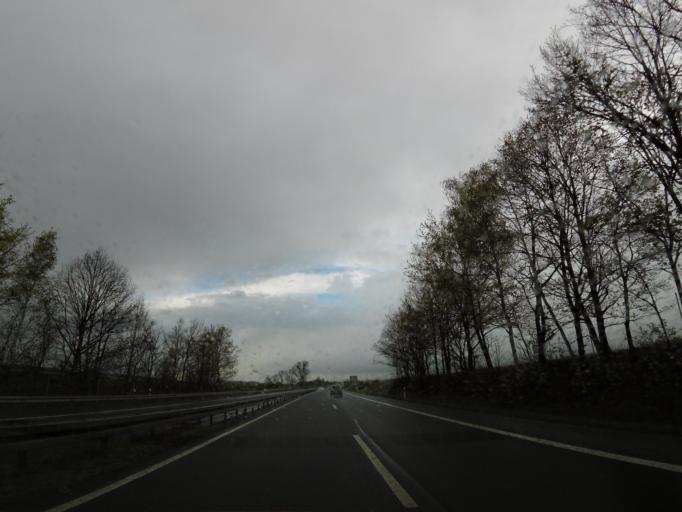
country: DE
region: Lower Saxony
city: Vienenburg
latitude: 51.9244
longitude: 10.5589
